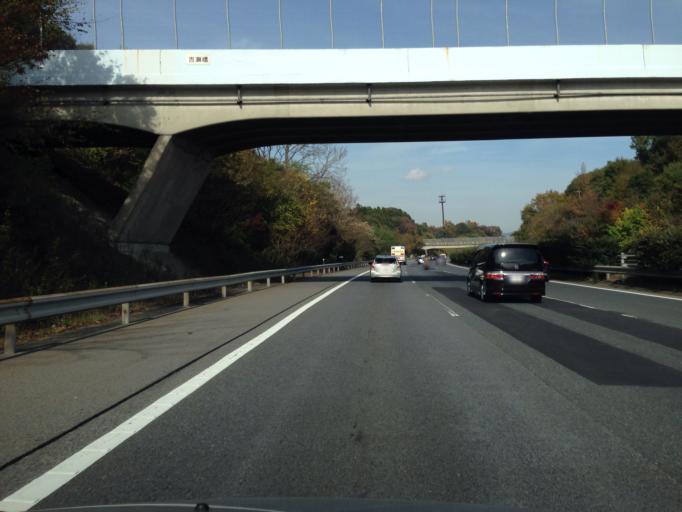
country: JP
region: Ibaraki
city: Naka
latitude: 36.0812
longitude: 140.1545
